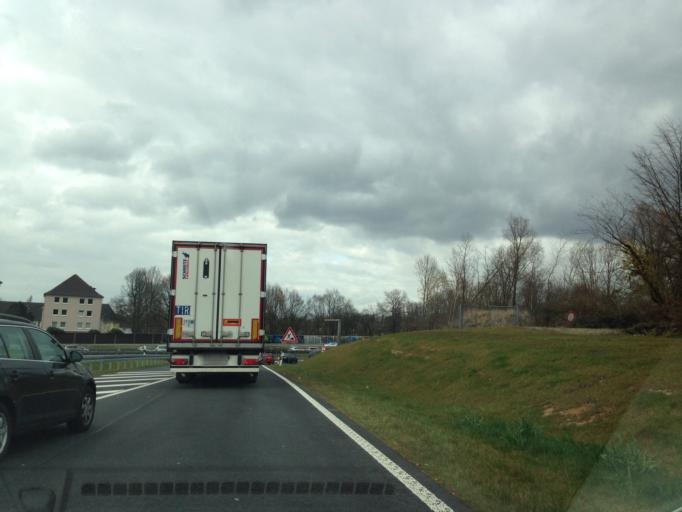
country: DE
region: North Rhine-Westphalia
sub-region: Regierungsbezirk Dusseldorf
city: Essen
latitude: 51.4532
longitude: 7.0411
